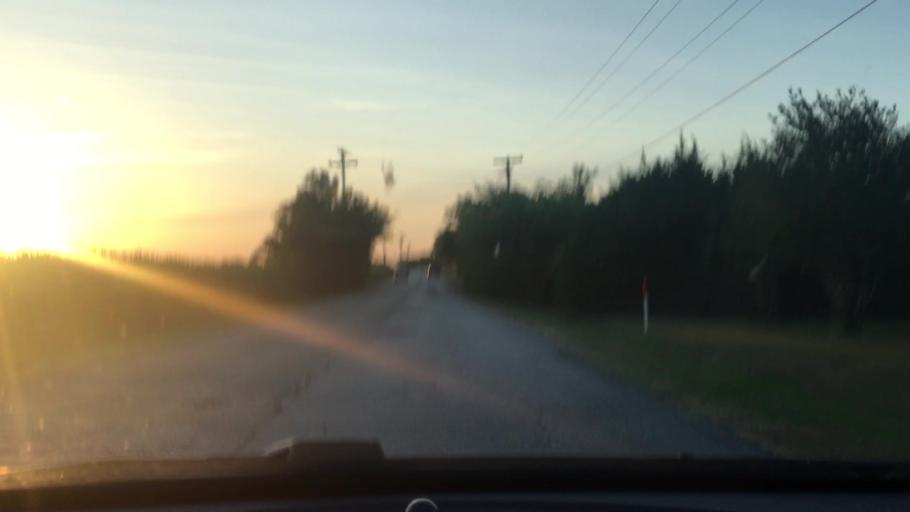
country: US
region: Texas
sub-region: Ellis County
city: Red Oak
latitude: 32.5607
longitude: -96.7935
